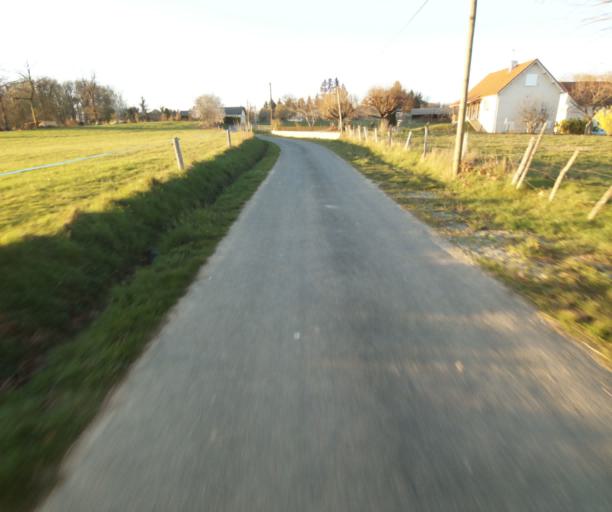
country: FR
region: Limousin
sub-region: Departement de la Correze
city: Saint-Mexant
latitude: 45.3141
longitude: 1.6569
